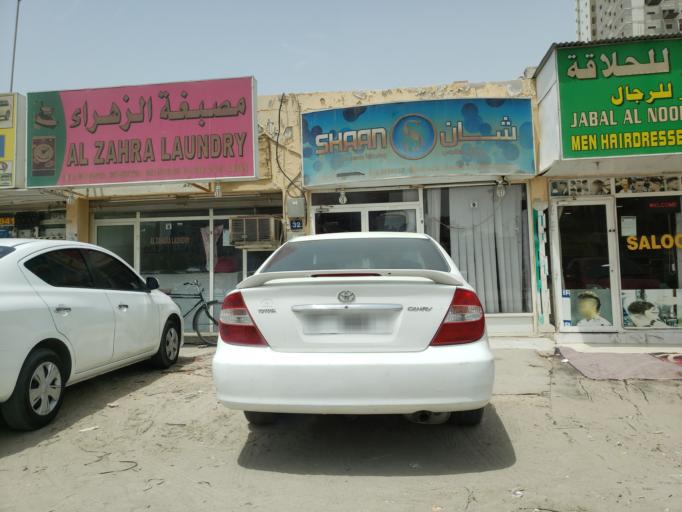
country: AE
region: Ajman
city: Ajman
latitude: 25.3918
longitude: 55.4622
